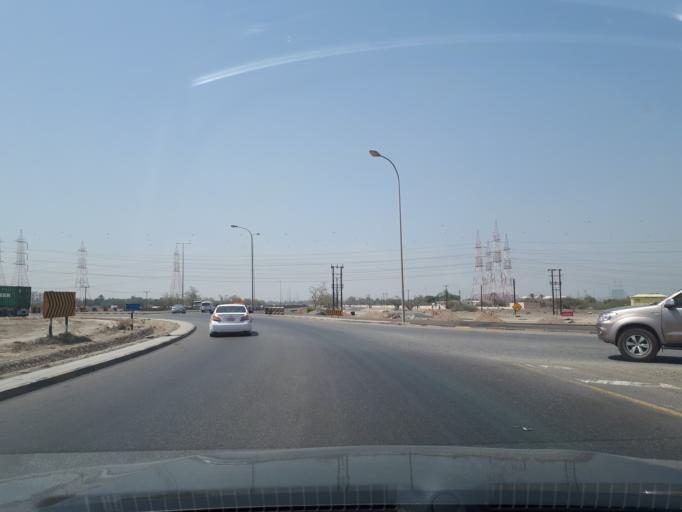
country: OM
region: Al Batinah
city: Al Liwa'
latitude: 24.4485
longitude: 56.6089
